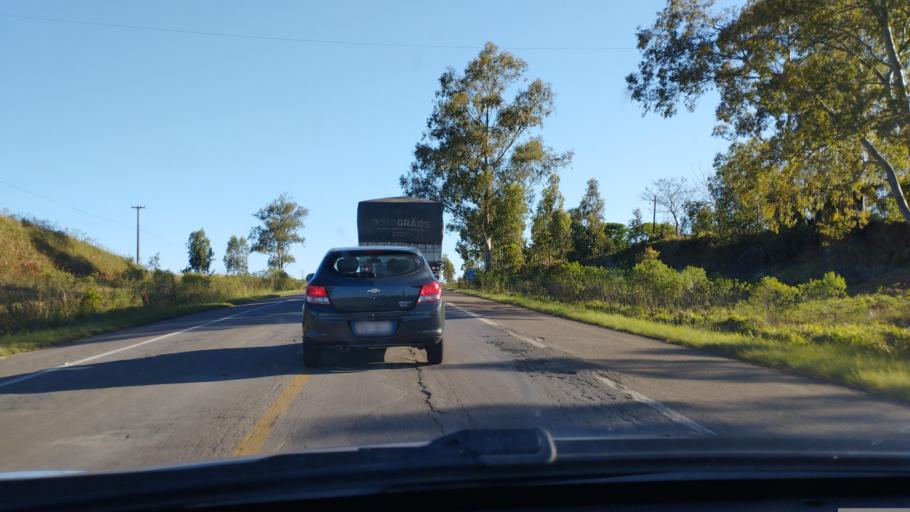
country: BR
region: Rio Grande do Sul
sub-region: Julio De Castilhos
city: Julio de Castilhos
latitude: -29.3764
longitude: -53.6707
